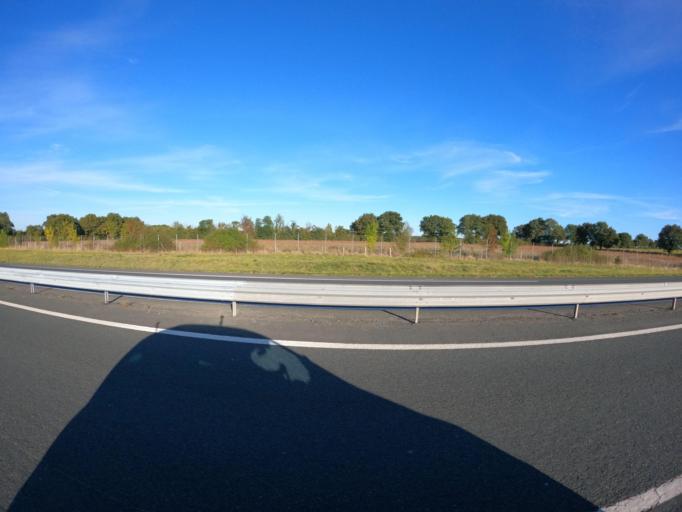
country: FR
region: Pays de la Loire
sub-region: Departement de Maine-et-Loire
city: Mazieres-en-Mauges
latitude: 47.0723
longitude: -0.8263
